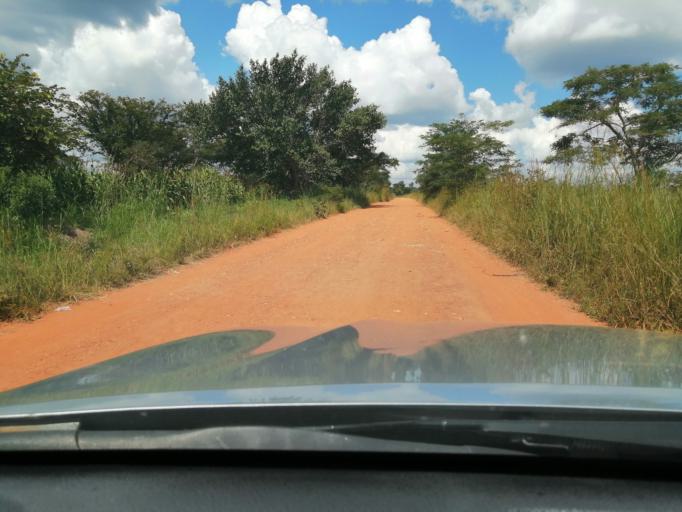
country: ZM
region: Lusaka
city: Lusaka
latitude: -15.1970
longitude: 27.9957
